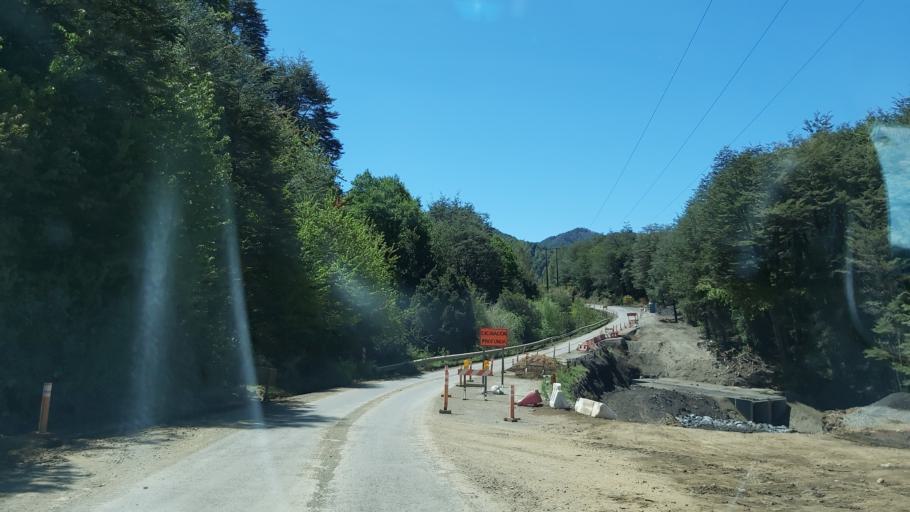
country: CL
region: Araucania
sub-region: Provincia de Cautin
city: Vilcun
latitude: -38.4725
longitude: -71.6787
